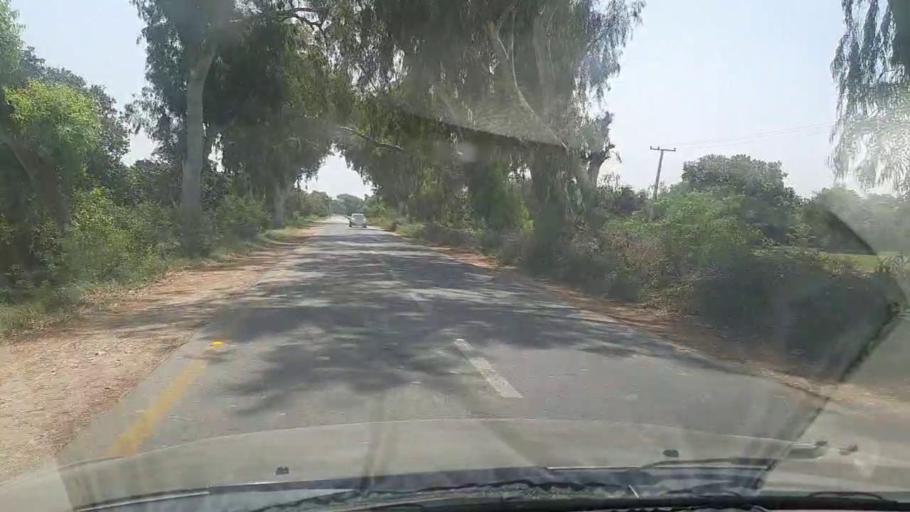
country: PK
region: Sindh
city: Tando Jam
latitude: 25.3464
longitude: 68.5153
